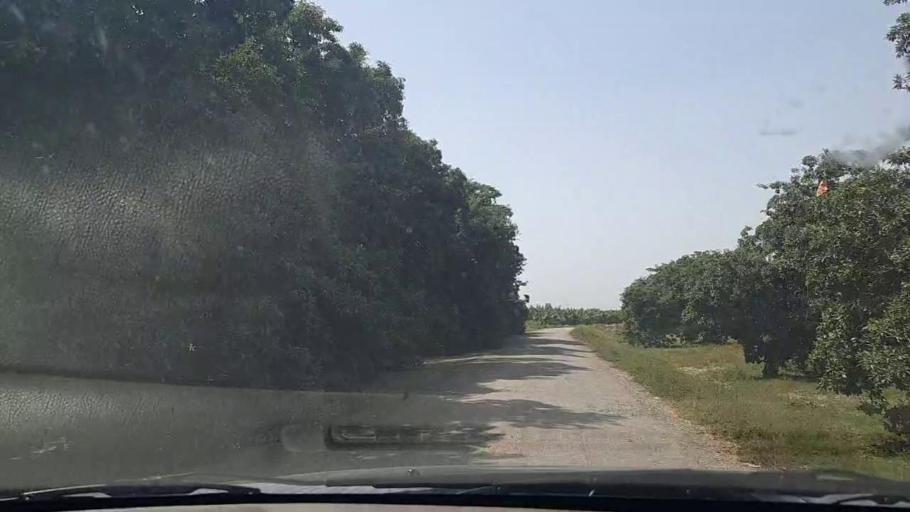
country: PK
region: Sindh
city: Keti Bandar
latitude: 24.2830
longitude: 67.6705
